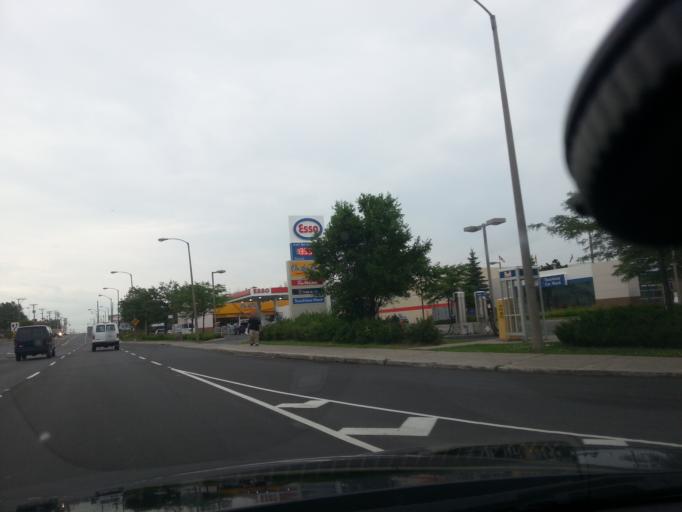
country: CA
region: Ontario
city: Ottawa
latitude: 45.3785
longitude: -75.6676
